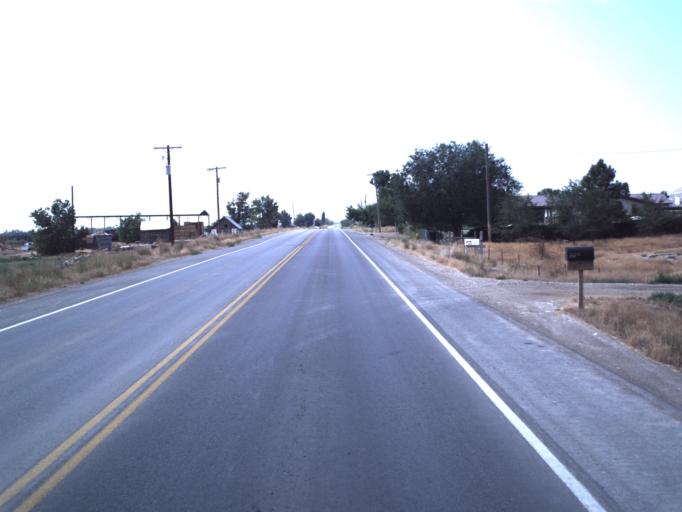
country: US
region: Utah
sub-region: Uintah County
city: Naples
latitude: 40.3862
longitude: -109.4987
